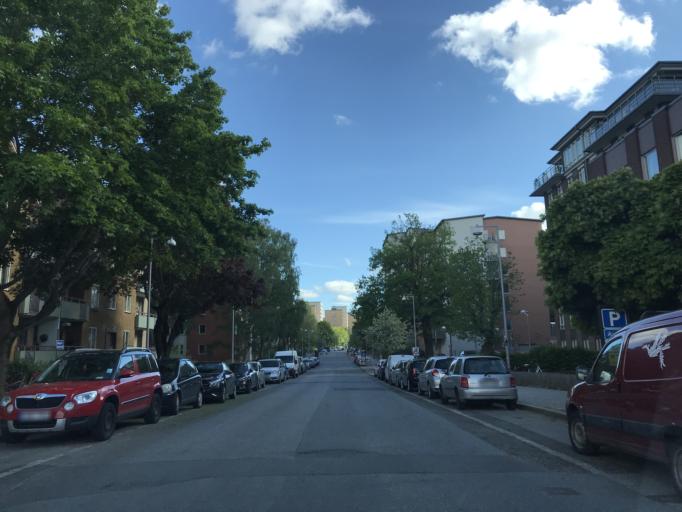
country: SE
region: Stockholm
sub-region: Solna Kommun
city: Solna
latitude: 59.3519
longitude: 17.9969
